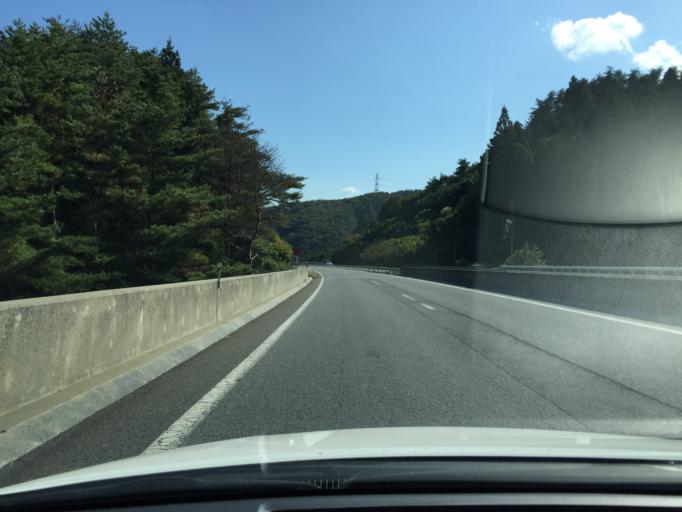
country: JP
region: Fukushima
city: Iwaki
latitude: 37.1574
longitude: 140.7328
